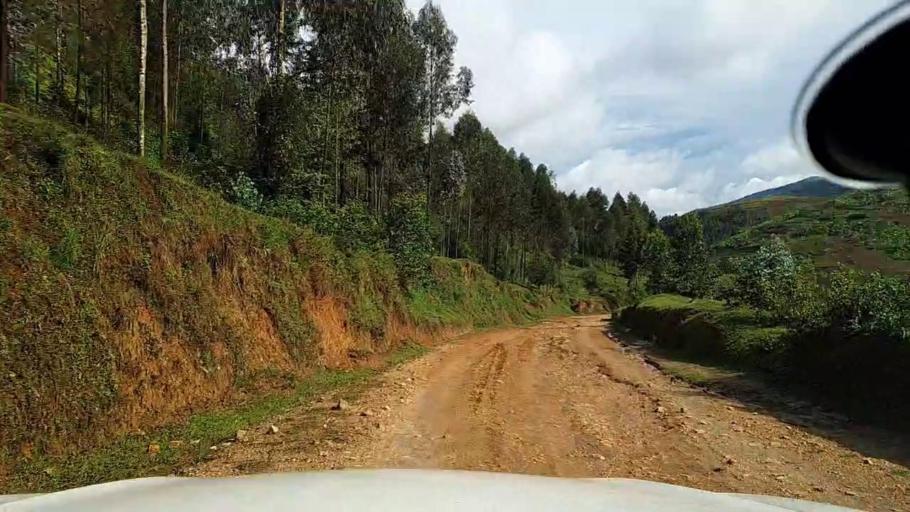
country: RW
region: Western Province
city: Kibuye
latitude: -2.1260
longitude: 29.4980
